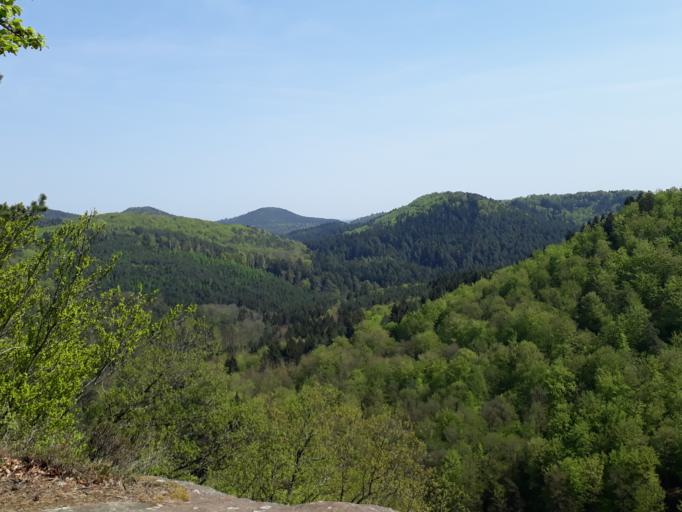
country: FR
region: Alsace
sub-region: Departement du Bas-Rhin
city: Neuwiller-les-Saverne
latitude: 48.8479
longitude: 7.3409
